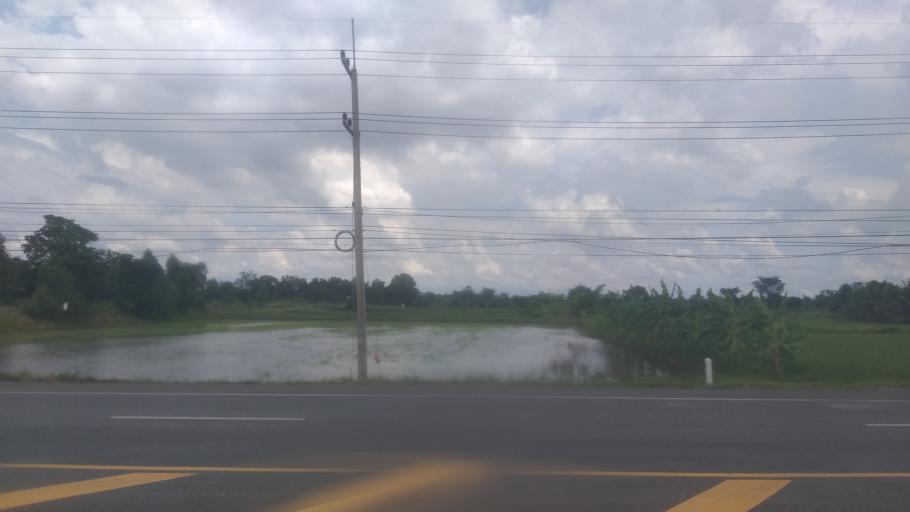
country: TH
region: Chaiyaphum
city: Noen Sa-nga
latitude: 15.6745
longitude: 101.9674
